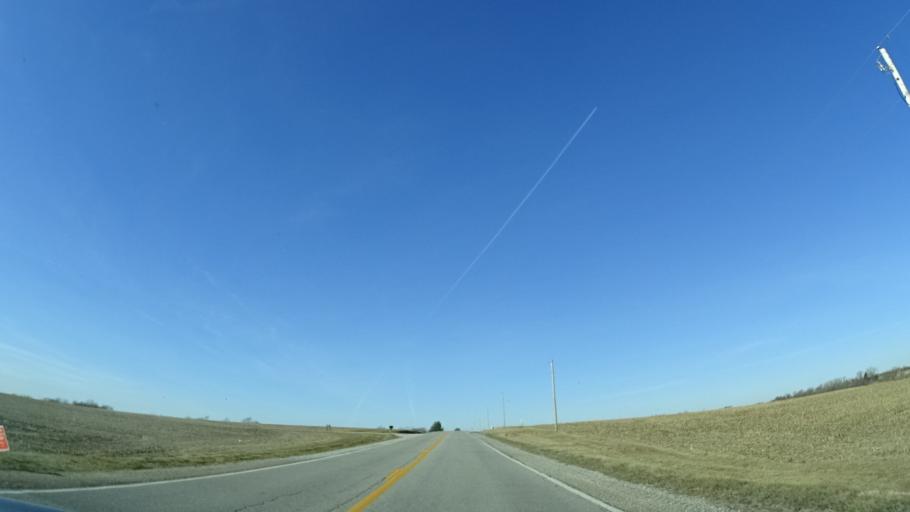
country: US
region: Nebraska
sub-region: Sarpy County
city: Papillion
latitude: 41.0890
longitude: -96.0556
